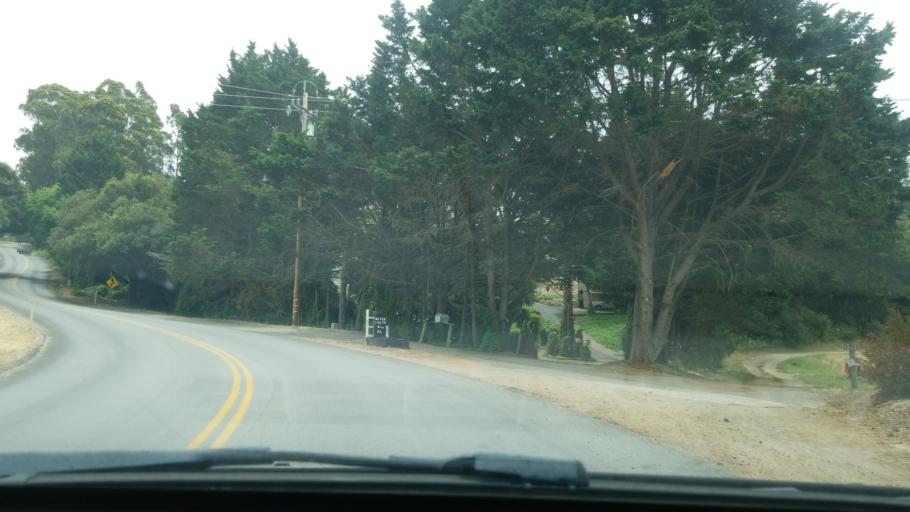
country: US
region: California
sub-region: San Luis Obispo County
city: Callender
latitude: 35.0759
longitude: -120.5432
